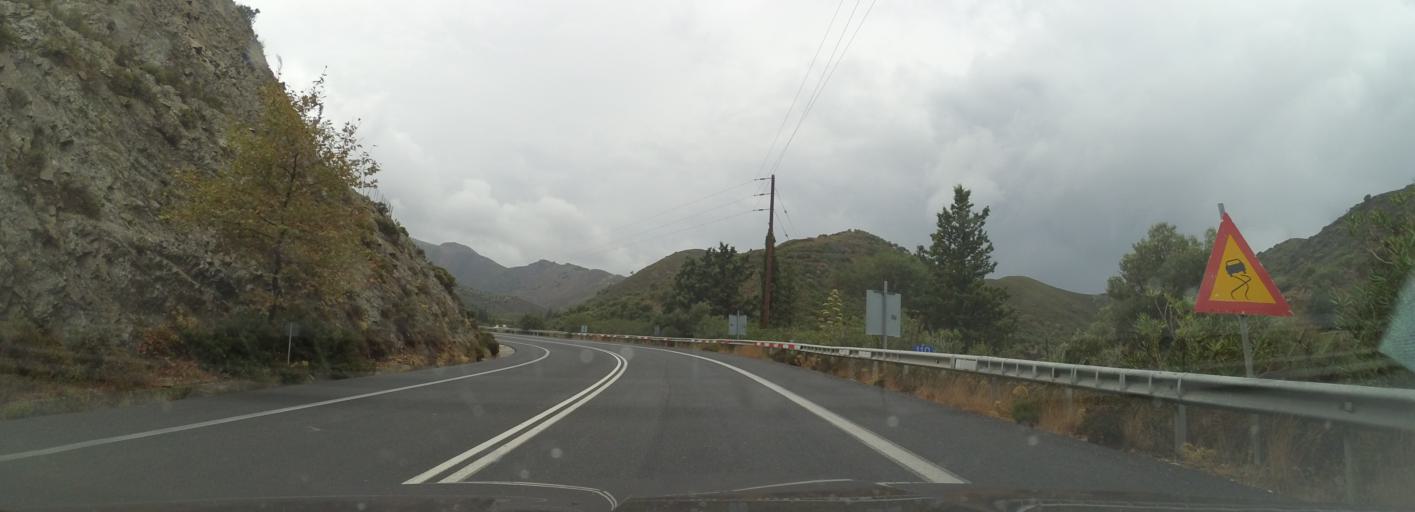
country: GR
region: Crete
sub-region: Nomos Irakleiou
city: Tilisos
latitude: 35.3925
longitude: 24.9469
